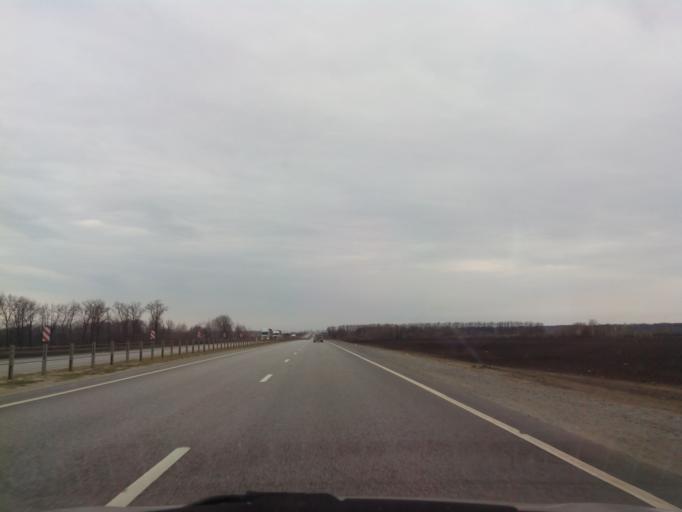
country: RU
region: Tambov
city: Zavoronezhskoye
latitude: 52.8988
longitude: 40.6689
